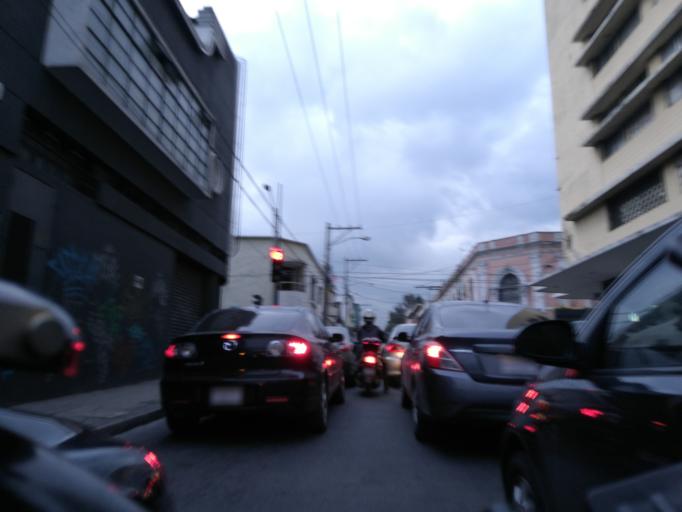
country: GT
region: Guatemala
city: Guatemala City
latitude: 14.6326
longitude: -90.5158
